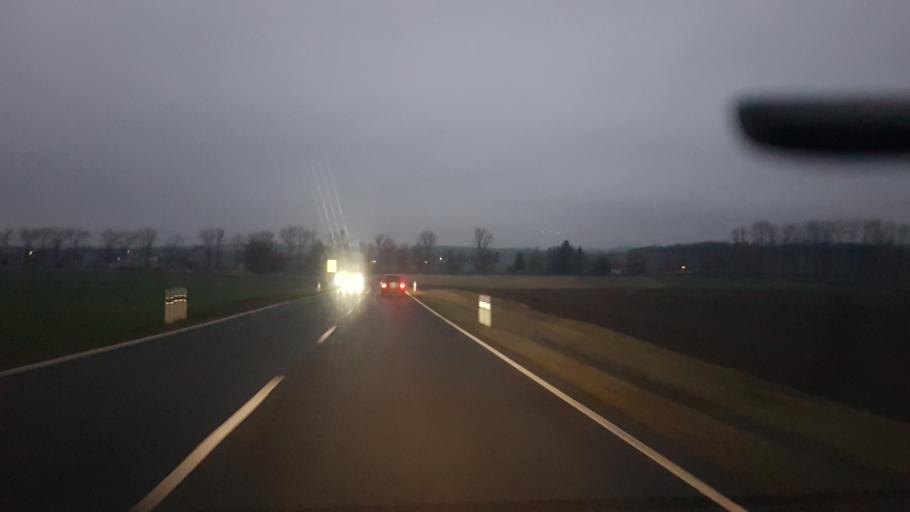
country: DE
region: Bavaria
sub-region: Regierungsbezirk Unterfranken
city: Bad Konigshofen im Grabfeld
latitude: 50.2902
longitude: 10.4867
